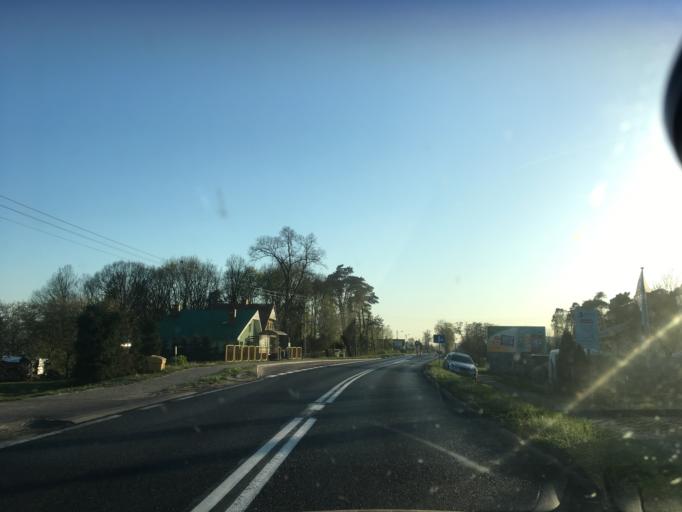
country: PL
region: Lubusz
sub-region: Powiat gorzowski
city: Jenin
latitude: 52.6948
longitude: 15.0929
